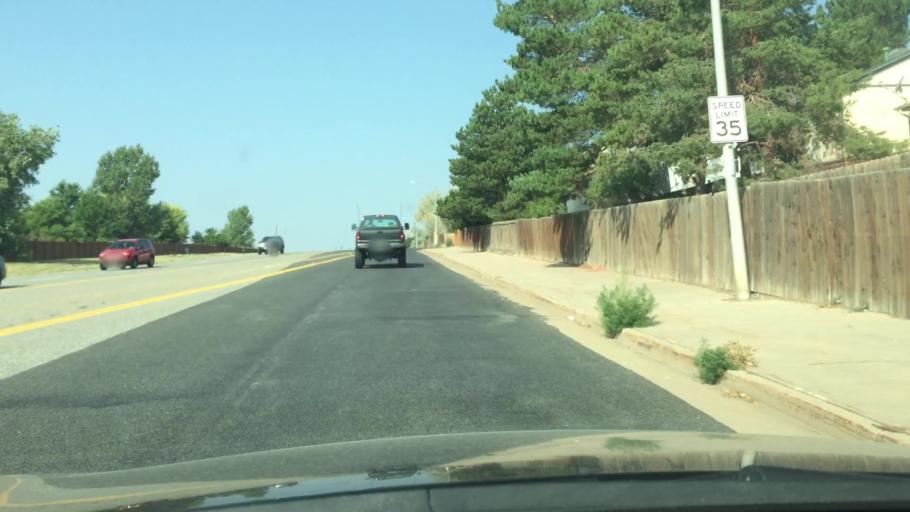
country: US
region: Colorado
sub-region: Arapahoe County
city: Dove Valley
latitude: 39.6386
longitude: -104.7556
